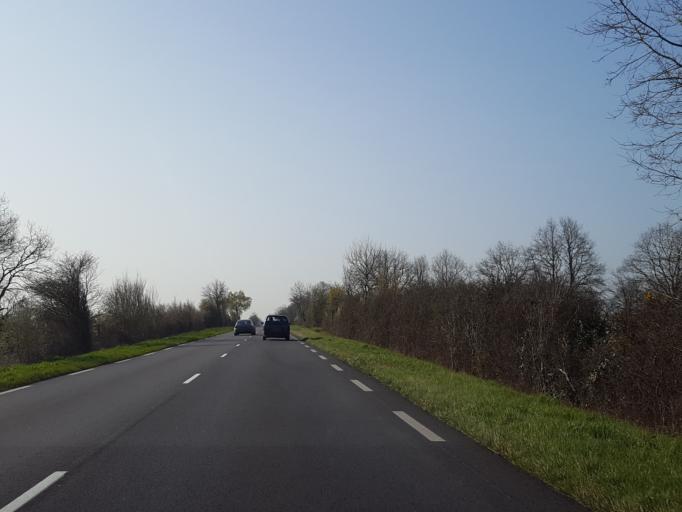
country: FR
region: Pays de la Loire
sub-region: Departement de la Loire-Atlantique
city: Geneston
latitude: 47.0326
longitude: -1.5062
